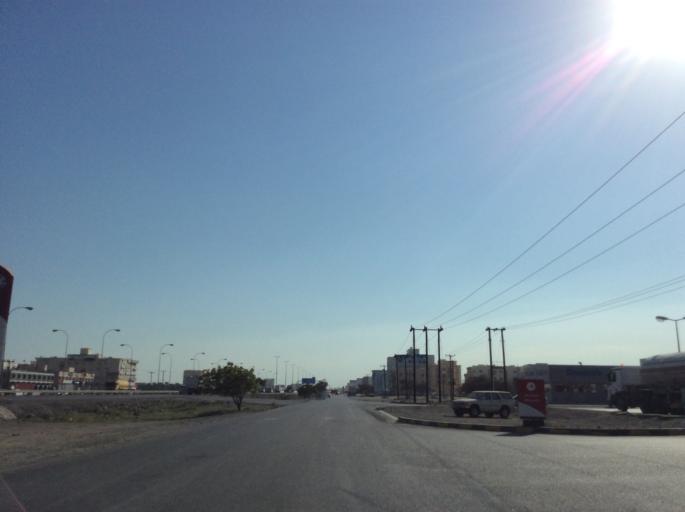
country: OM
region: Al Batinah
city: Al Liwa'
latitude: 24.4434
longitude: 56.6077
